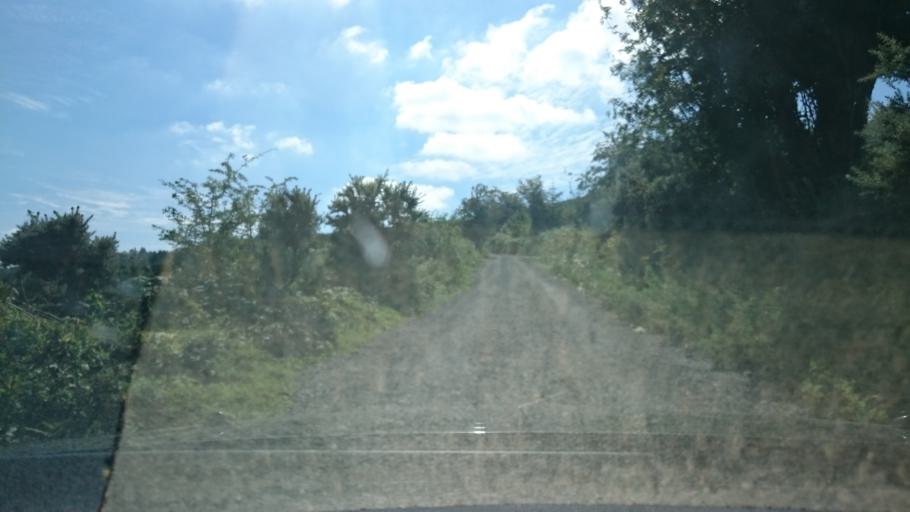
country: IE
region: Leinster
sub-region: Kilkenny
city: Graiguenamanagh
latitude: 52.5227
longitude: -6.9640
